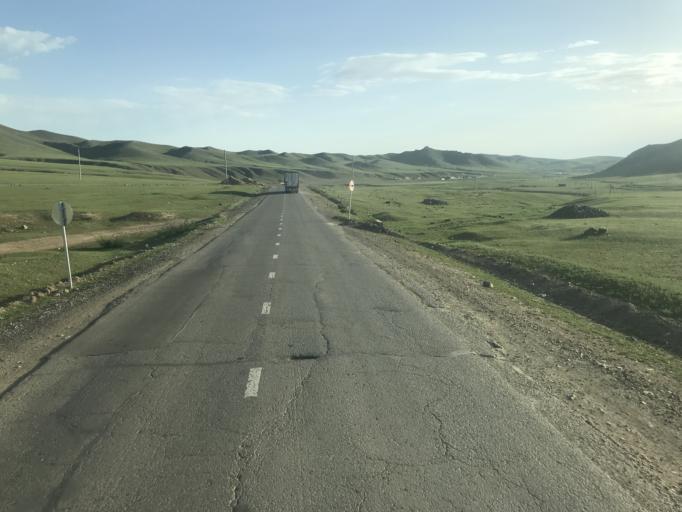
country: MN
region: Central Aimak
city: Bornuur
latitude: 48.4302
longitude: 106.1930
